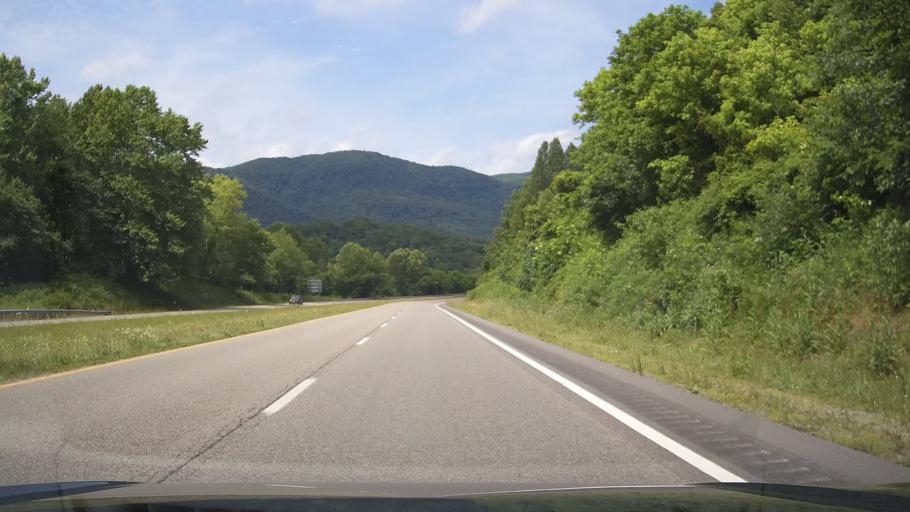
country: US
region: Virginia
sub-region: Wise County
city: Big Stone Gap
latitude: 36.8657
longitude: -82.7512
